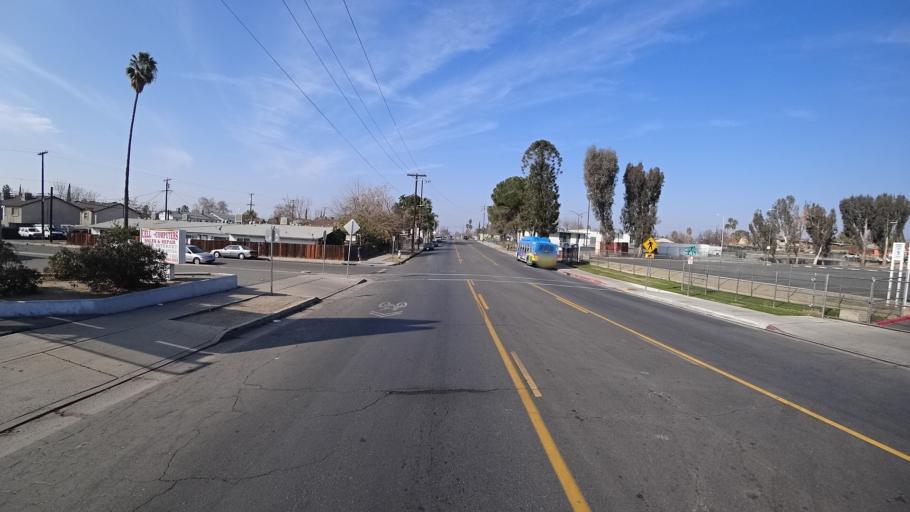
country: US
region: California
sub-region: Kern County
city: Bakersfield
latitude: 35.3820
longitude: -118.9723
